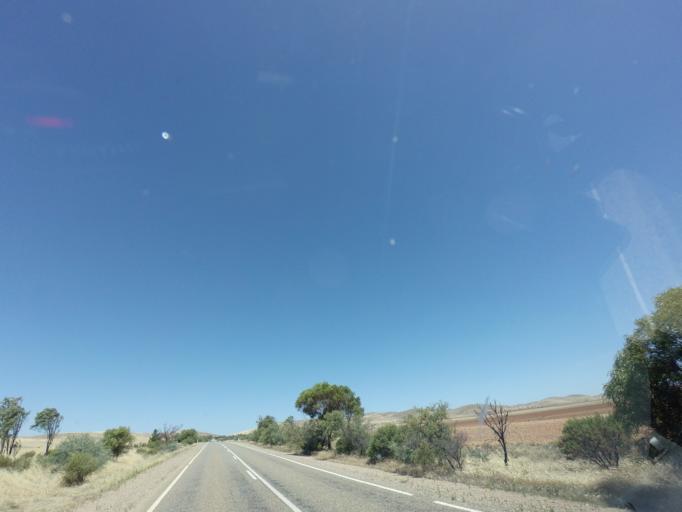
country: AU
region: South Australia
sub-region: Peterborough
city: Peterborough
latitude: -32.7243
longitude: 138.5151
